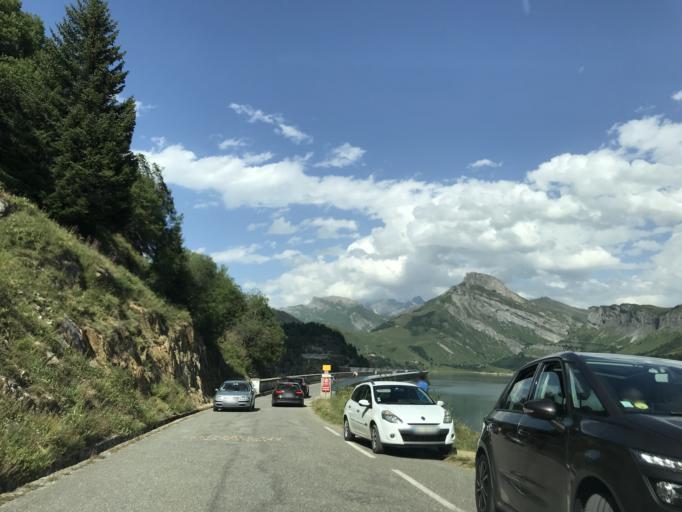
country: FR
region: Rhone-Alpes
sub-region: Departement de la Savoie
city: Beaufort
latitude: 45.6824
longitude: 6.6167
